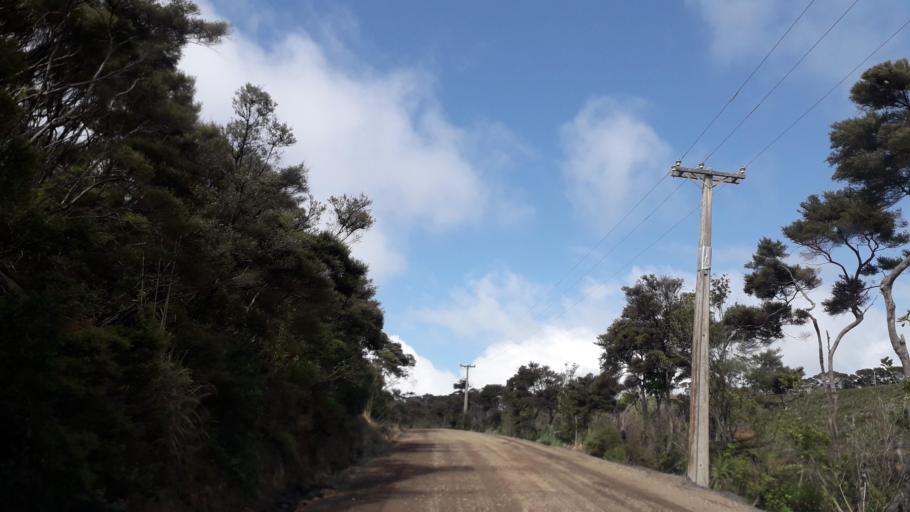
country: NZ
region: Northland
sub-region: Far North District
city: Paihia
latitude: -35.2409
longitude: 174.2480
